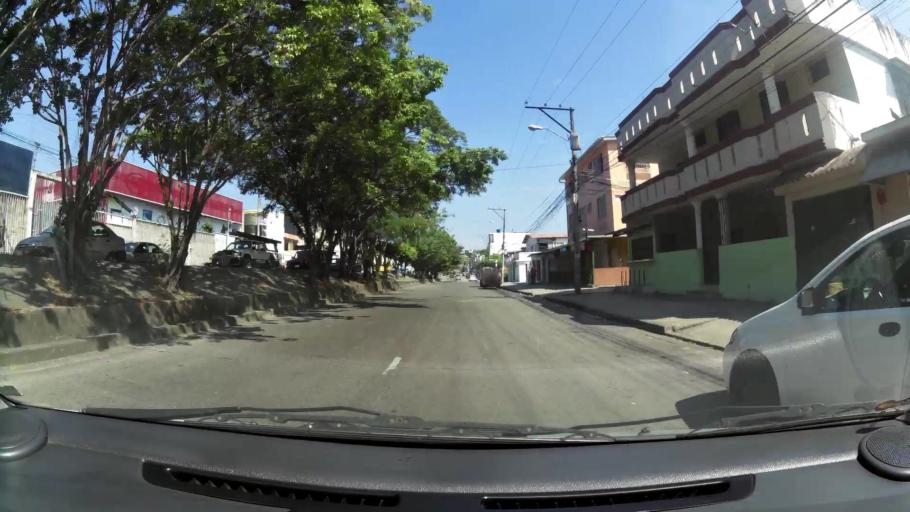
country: EC
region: Guayas
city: Eloy Alfaro
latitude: -2.1315
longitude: -79.9083
